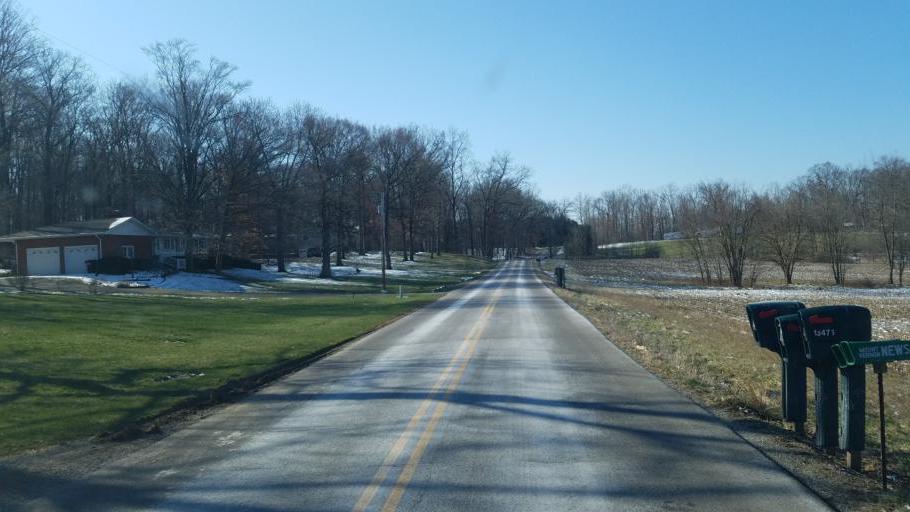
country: US
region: Ohio
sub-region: Knox County
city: Fredericktown
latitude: 40.4599
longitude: -82.4851
